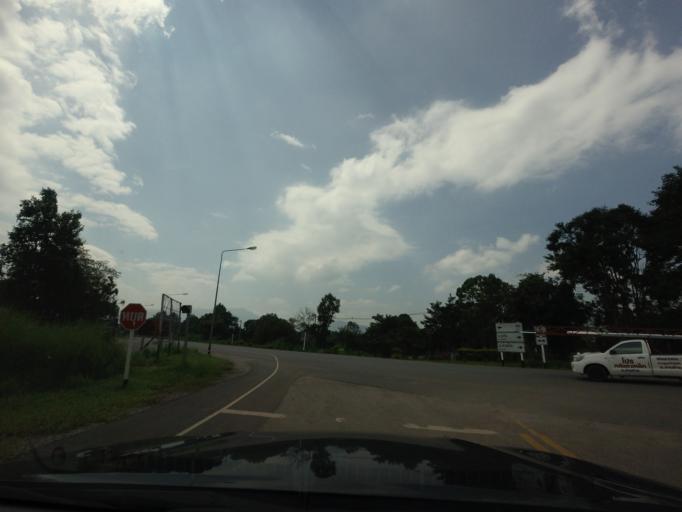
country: TH
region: Loei
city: Phu Ruea
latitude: 17.4463
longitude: 101.4669
